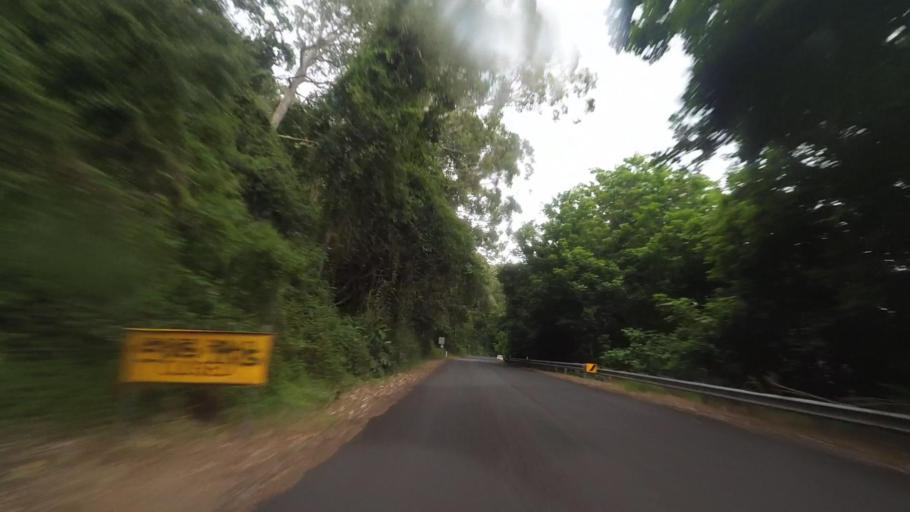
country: AU
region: New South Wales
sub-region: Wollongong
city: Cordeaux Heights
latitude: -34.4209
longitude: 150.8167
